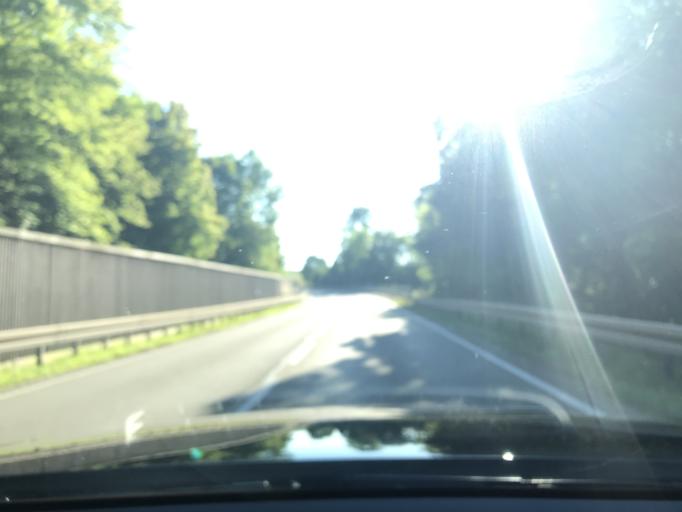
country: DE
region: Baden-Wuerttemberg
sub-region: Regierungsbezirk Stuttgart
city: Stuttgart Muehlhausen
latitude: 48.8477
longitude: 9.2573
